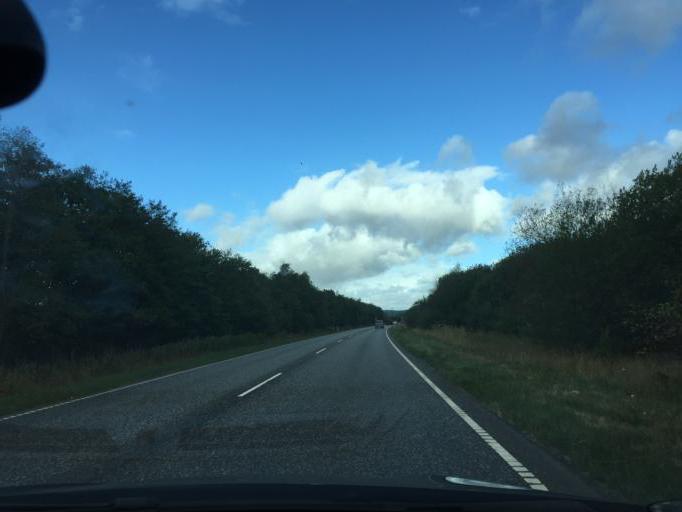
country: DK
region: South Denmark
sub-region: Vejle Kommune
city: Vejle
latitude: 55.7044
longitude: 9.5065
